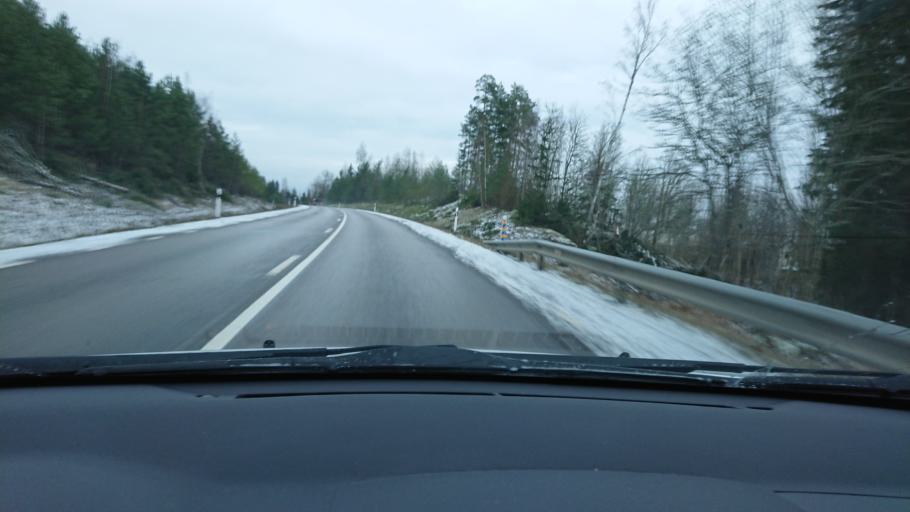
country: SE
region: Kalmar
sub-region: Hultsfreds Kommun
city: Virserum
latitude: 57.3677
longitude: 15.6761
